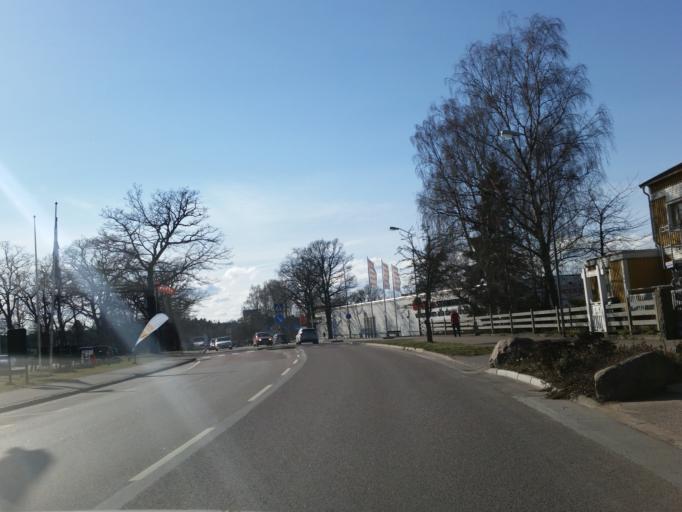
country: SE
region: Kalmar
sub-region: Oskarshamns Kommun
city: Oskarshamn
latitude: 57.2653
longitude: 16.4349
